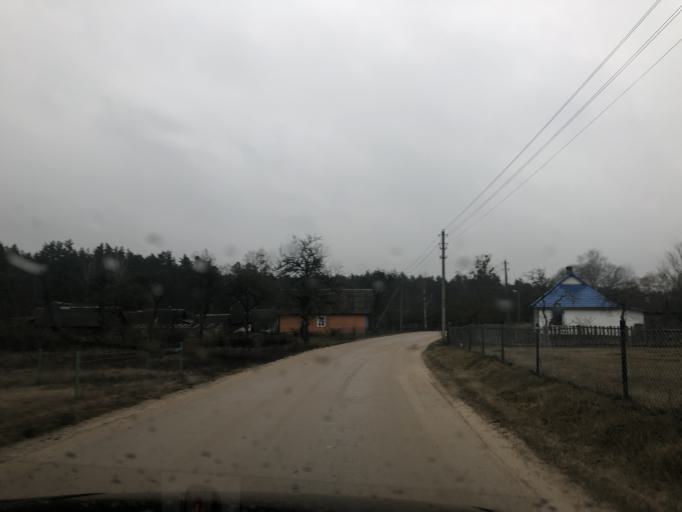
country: BY
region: Grodnenskaya
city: Skidal'
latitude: 53.8589
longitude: 24.2503
